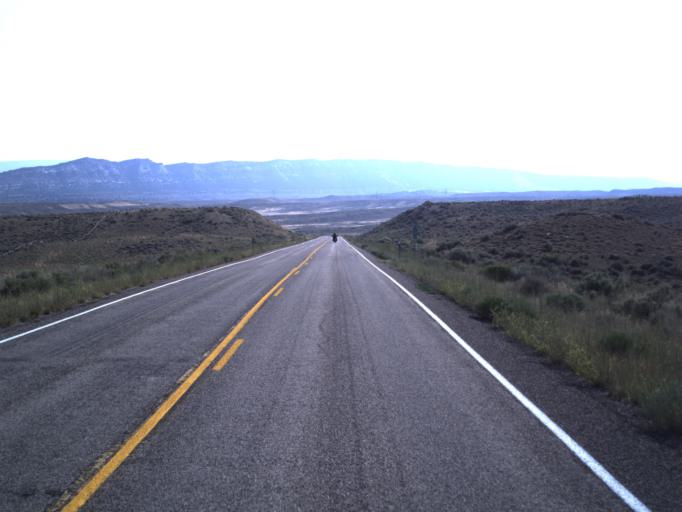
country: US
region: Utah
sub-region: Daggett County
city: Manila
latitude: 40.9770
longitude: -109.4575
